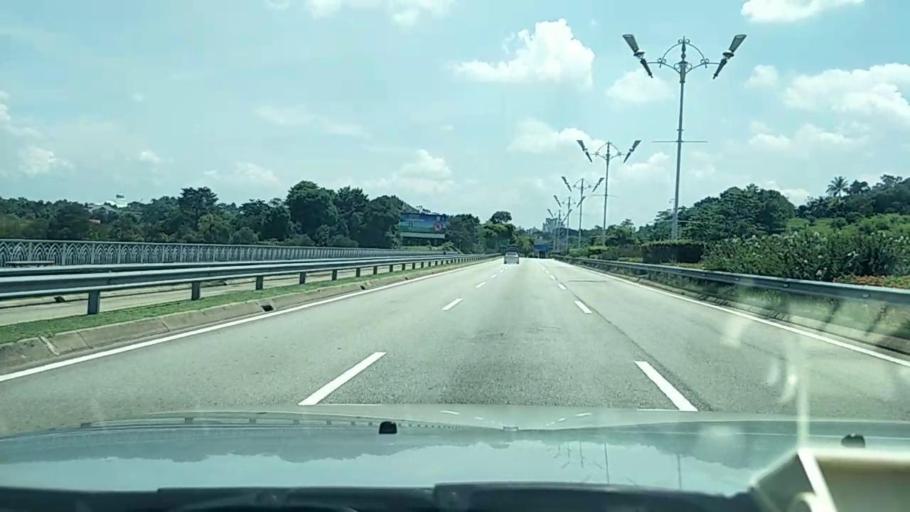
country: MY
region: Putrajaya
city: Putrajaya
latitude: 2.9546
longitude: 101.6973
